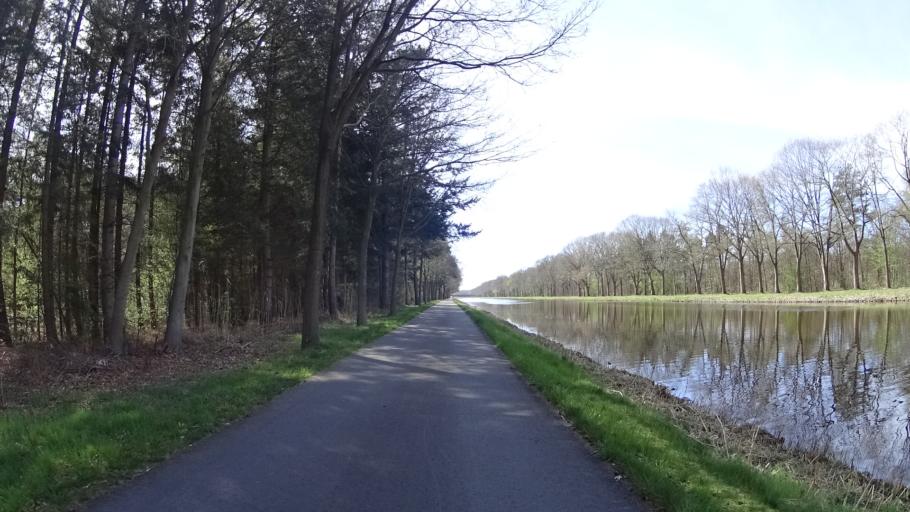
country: DE
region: Lower Saxony
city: Geeste
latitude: 52.6096
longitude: 7.3084
